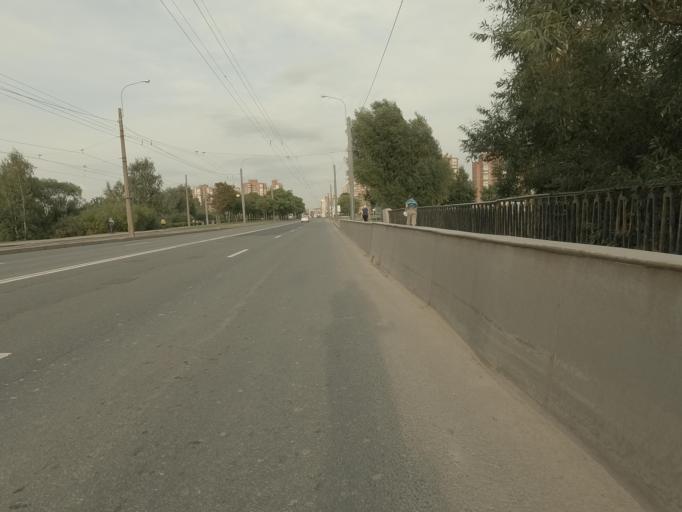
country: RU
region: St.-Petersburg
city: Uritsk
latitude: 59.8330
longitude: 30.1865
